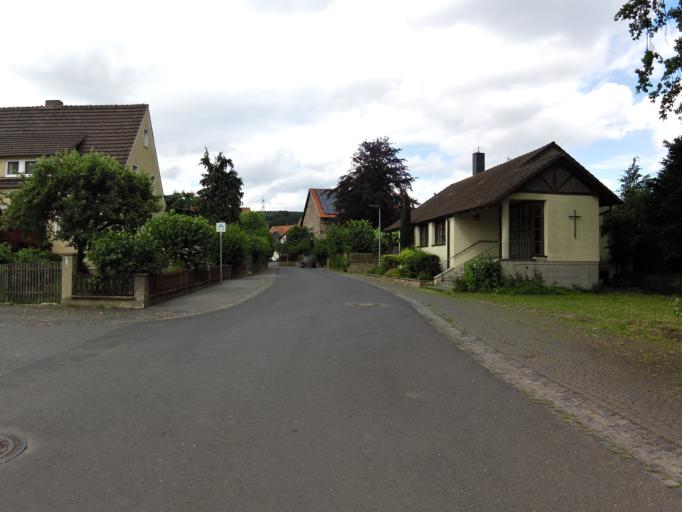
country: DE
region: Thuringia
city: Lauchroden
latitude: 51.0048
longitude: 10.1602
